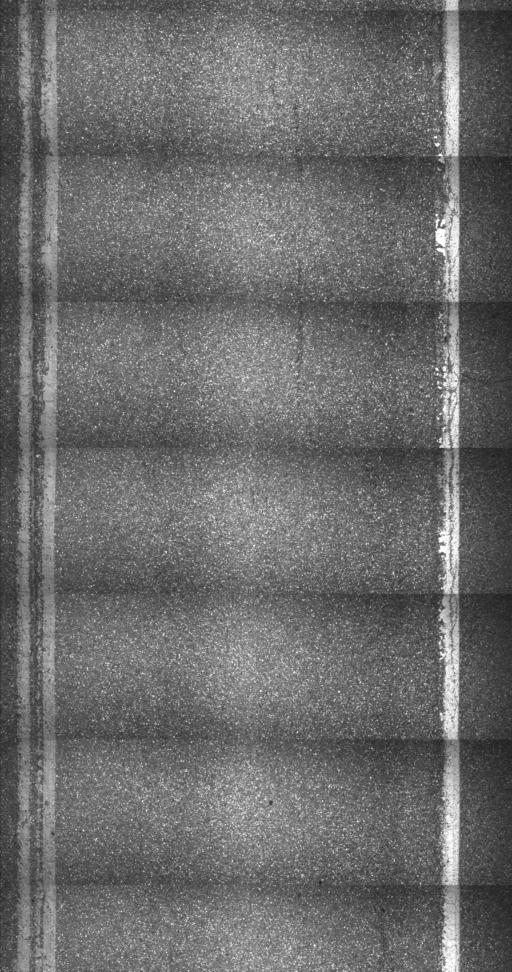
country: US
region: Vermont
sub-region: Lamoille County
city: Morrisville
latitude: 44.5562
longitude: -72.4846
